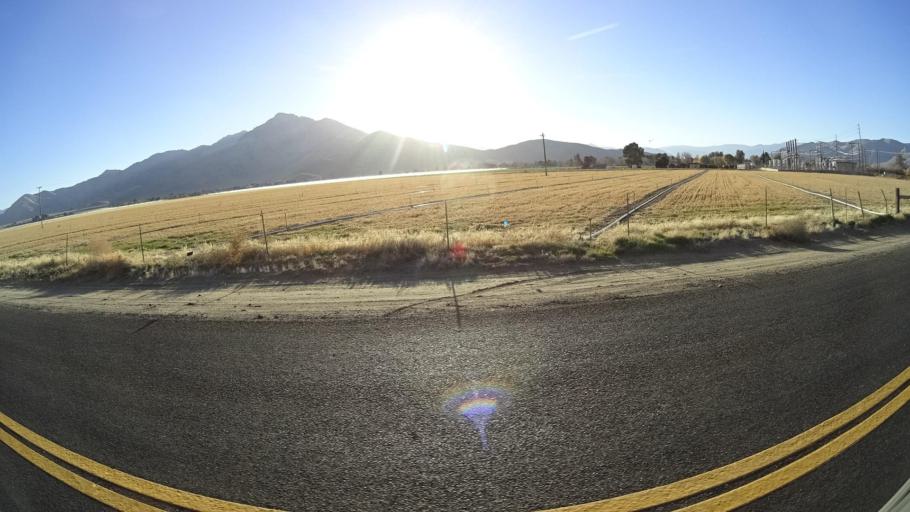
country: US
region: California
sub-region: Kern County
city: Weldon
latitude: 35.6662
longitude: -118.2604
